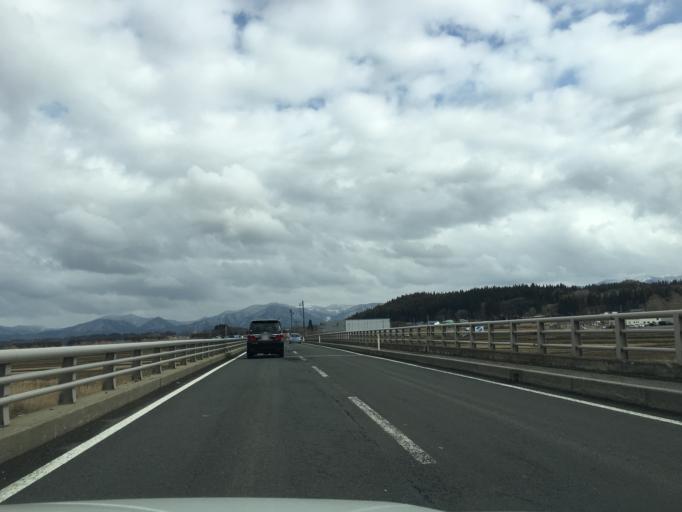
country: JP
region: Akita
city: Hanawa
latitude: 40.2473
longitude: 140.7499
